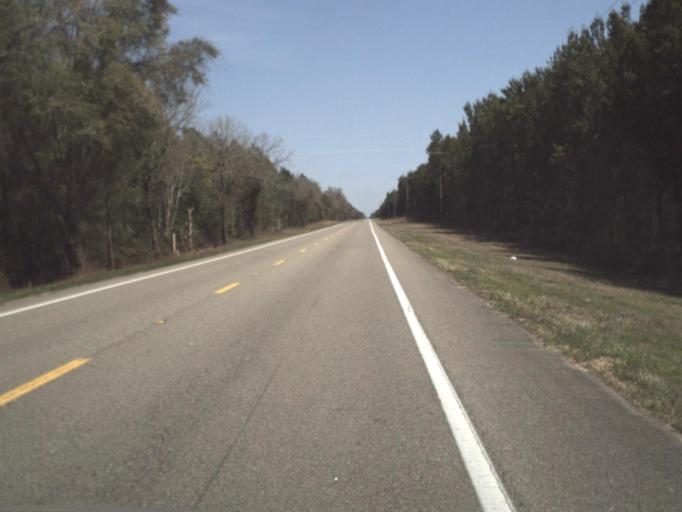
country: US
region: Florida
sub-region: Liberty County
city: Bristol
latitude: 30.4774
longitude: -84.9255
